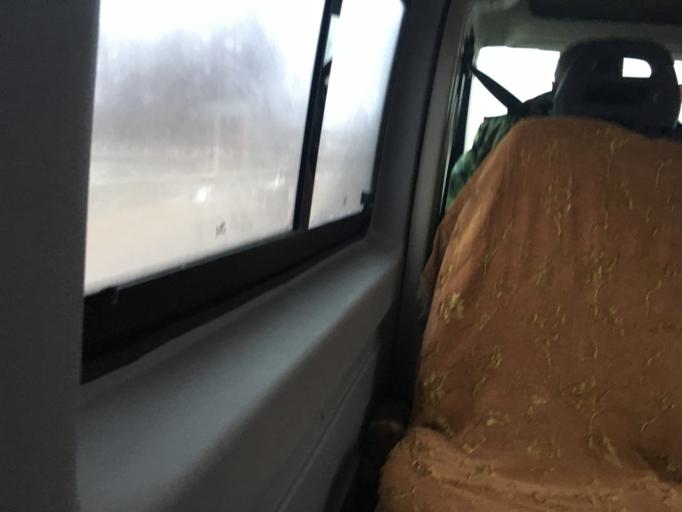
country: RU
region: Tula
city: Dubna
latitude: 54.0653
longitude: 37.0396
